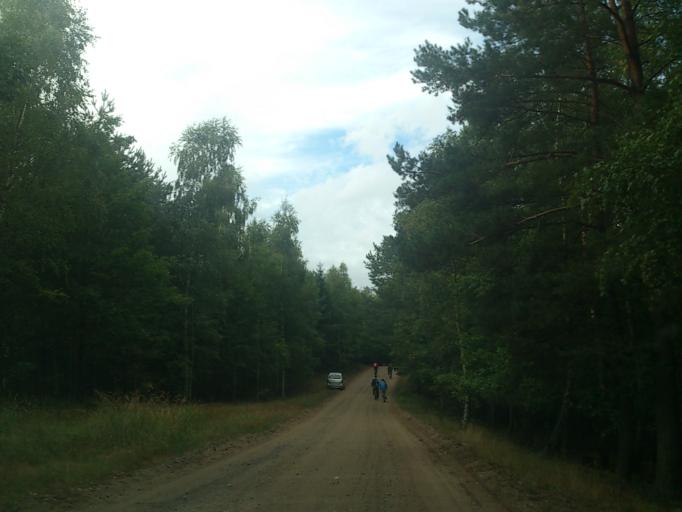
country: PL
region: Greater Poland Voivodeship
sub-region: Powiat poznanski
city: Kobylnica
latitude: 52.5281
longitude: 17.1180
